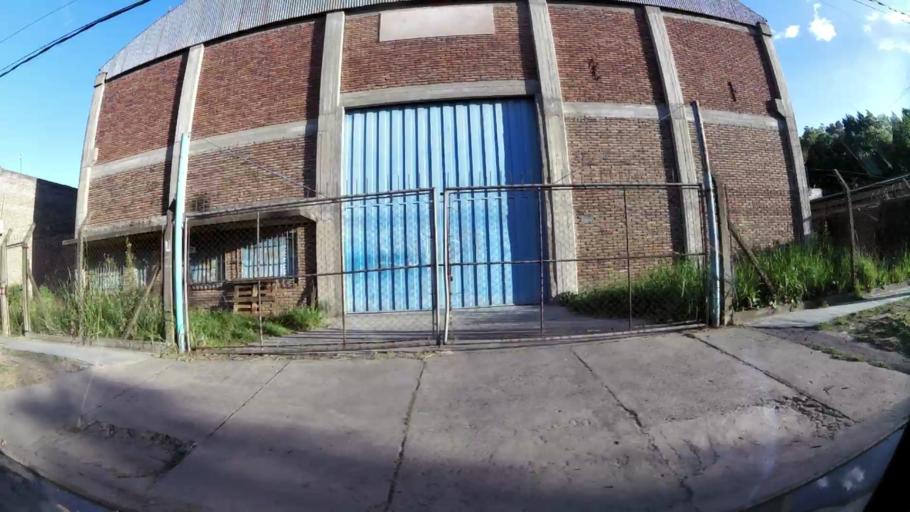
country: AR
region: Buenos Aires
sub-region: Partido de San Isidro
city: San Isidro
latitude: -34.4636
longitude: -58.5471
